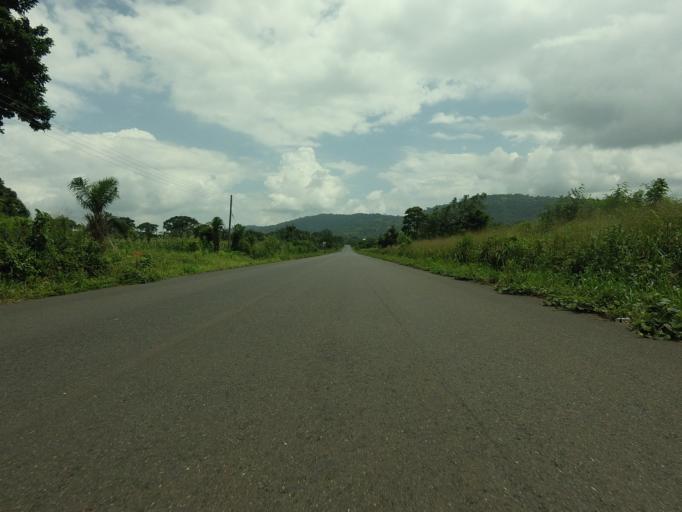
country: GH
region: Volta
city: Ho
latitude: 6.5414
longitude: 0.2438
